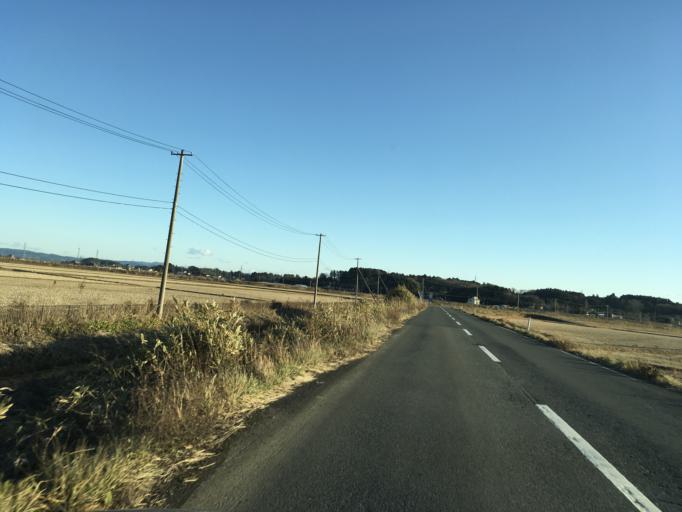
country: JP
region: Miyagi
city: Wakuya
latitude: 38.7257
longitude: 141.1288
